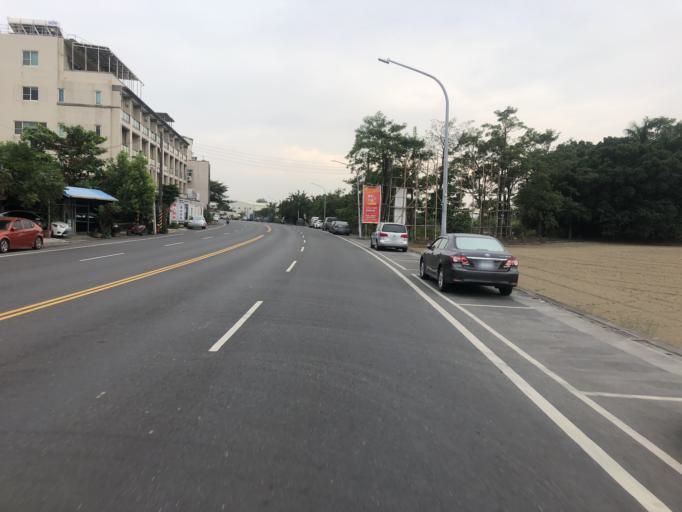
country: TW
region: Taiwan
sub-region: Tainan
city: Tainan
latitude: 23.1315
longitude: 120.2848
